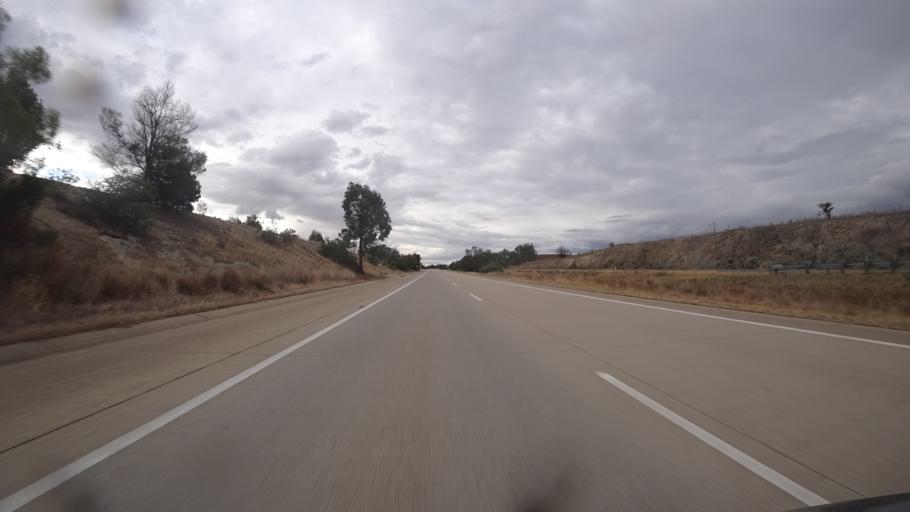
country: AU
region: New South Wales
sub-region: Yass Valley
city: Yass
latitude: -34.8007
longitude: 148.6937
